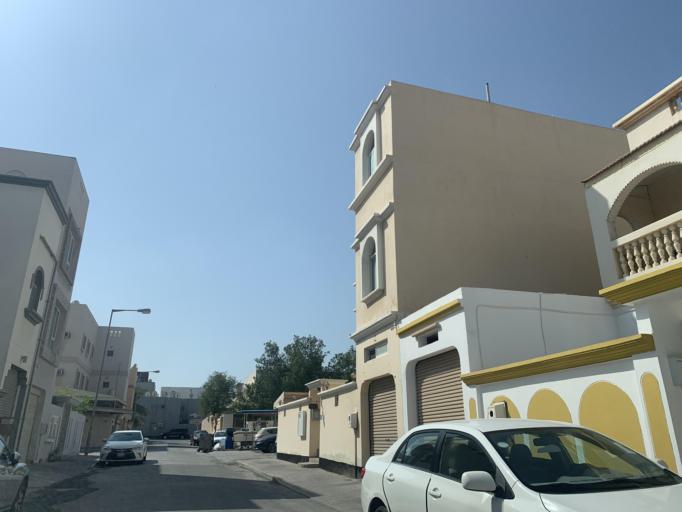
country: BH
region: Central Governorate
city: Madinat Hamad
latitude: 26.1390
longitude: 50.5067
